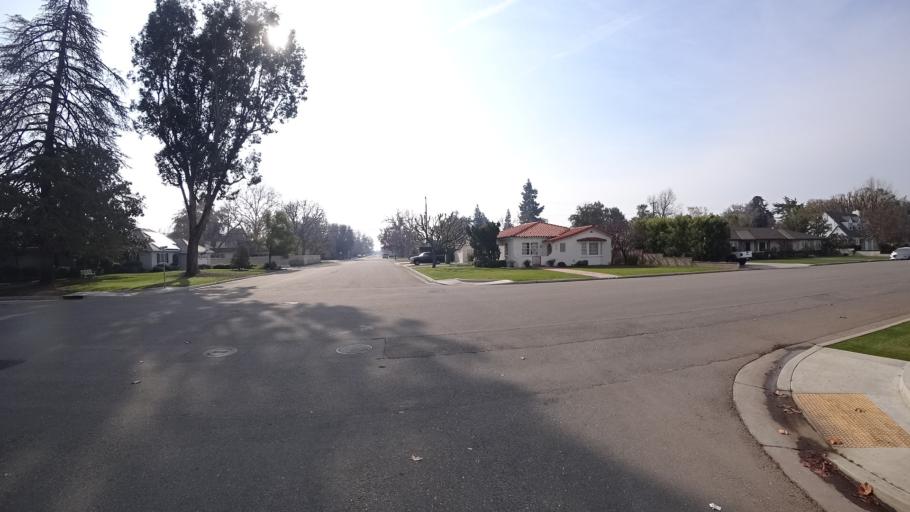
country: US
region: California
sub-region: Kern County
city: Bakersfield
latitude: 35.3792
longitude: -119.0341
